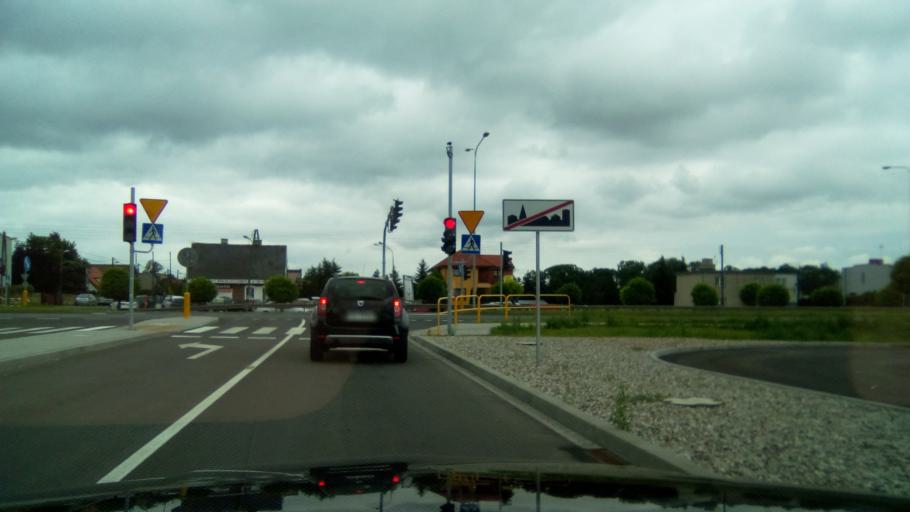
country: PL
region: Greater Poland Voivodeship
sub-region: Powiat gnieznienski
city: Gniezno
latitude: 52.5330
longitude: 17.5571
